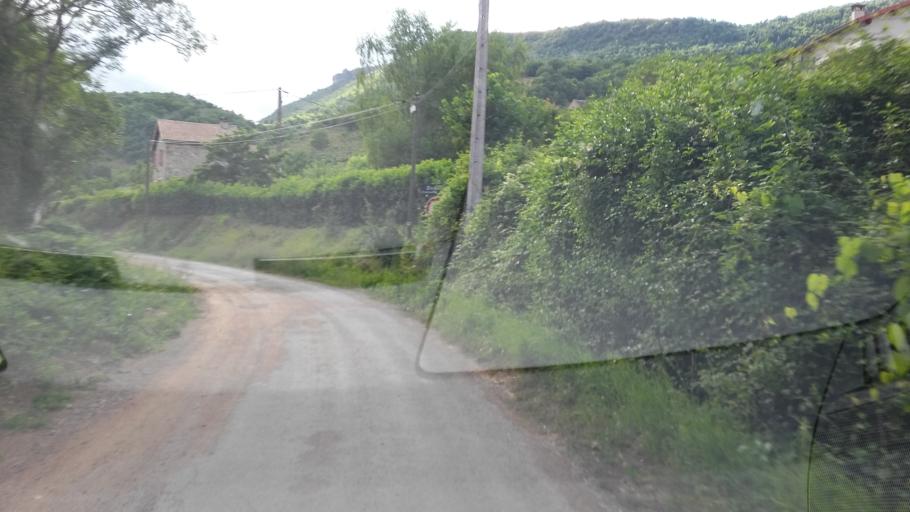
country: FR
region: Midi-Pyrenees
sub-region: Departement de l'Aveyron
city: La Cavalerie
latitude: 44.0246
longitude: 3.3344
